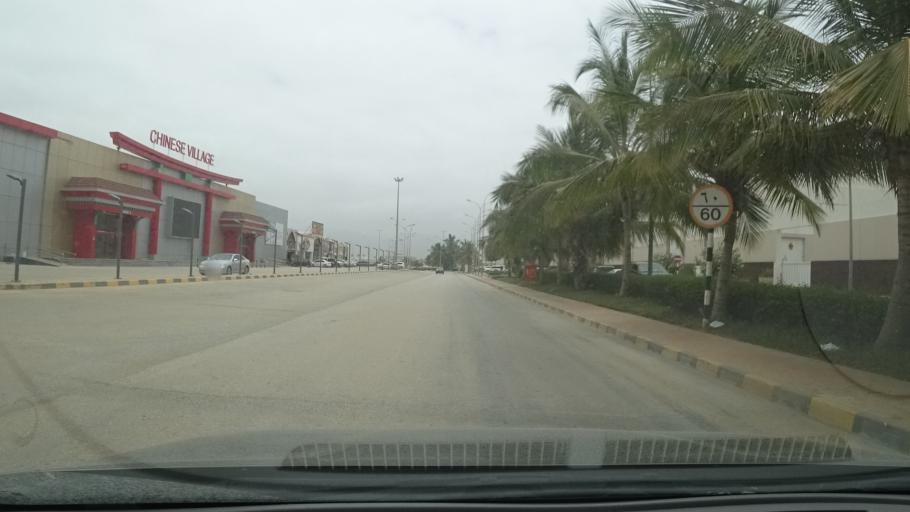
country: OM
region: Zufar
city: Salalah
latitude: 17.0216
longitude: 54.0653
